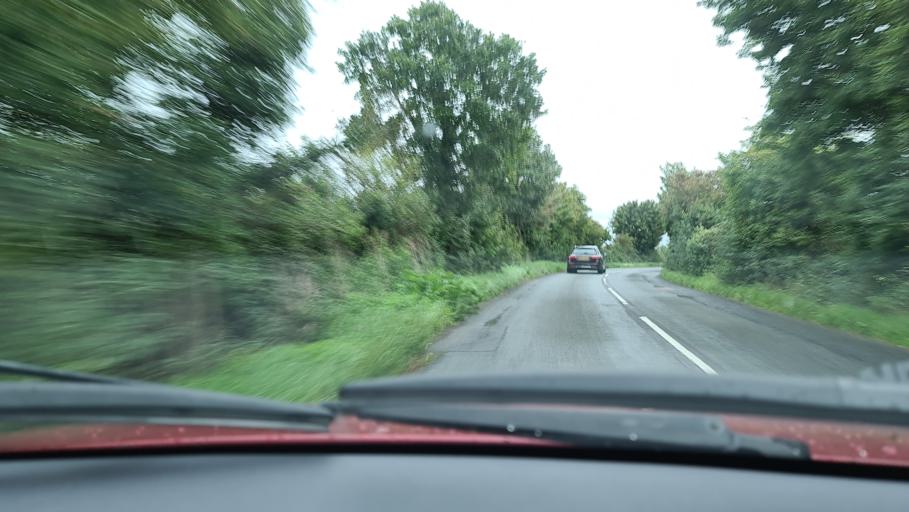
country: GB
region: England
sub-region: Oxfordshire
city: Somerton
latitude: 51.9430
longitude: -1.2083
